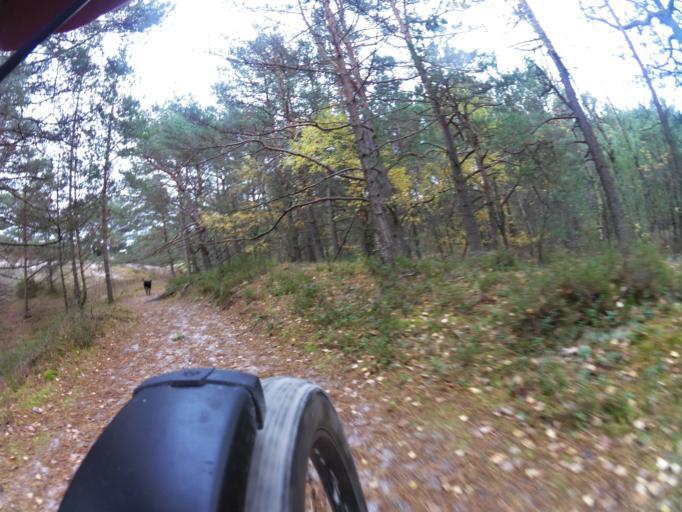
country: PL
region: Pomeranian Voivodeship
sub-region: Powiat leborski
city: Leba
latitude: 54.7703
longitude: 17.5920
